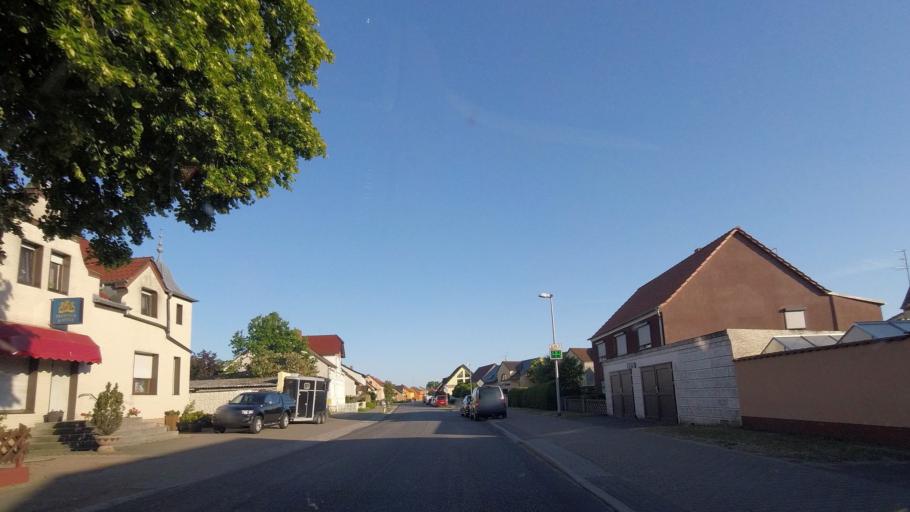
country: DE
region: Brandenburg
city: Golzow
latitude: 52.2809
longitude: 12.6044
